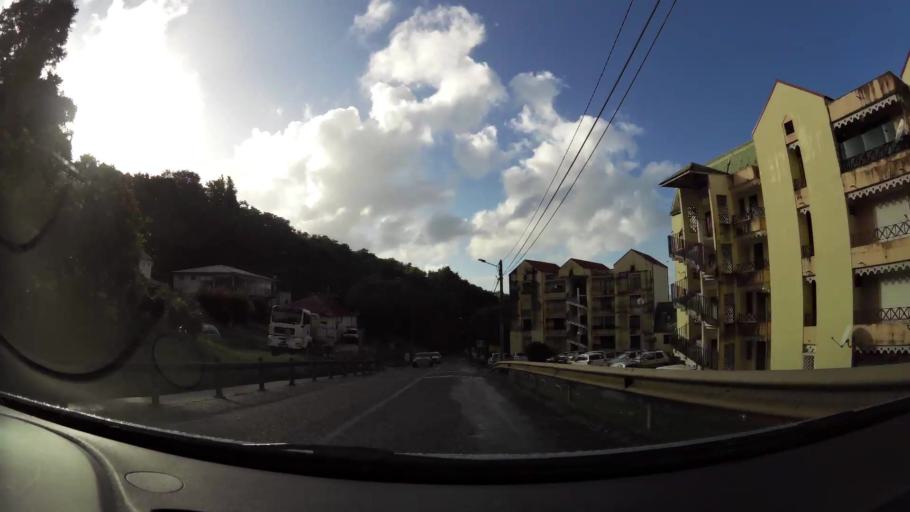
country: MQ
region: Martinique
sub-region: Martinique
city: Saint-Joseph
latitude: 14.6336
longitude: -61.0409
